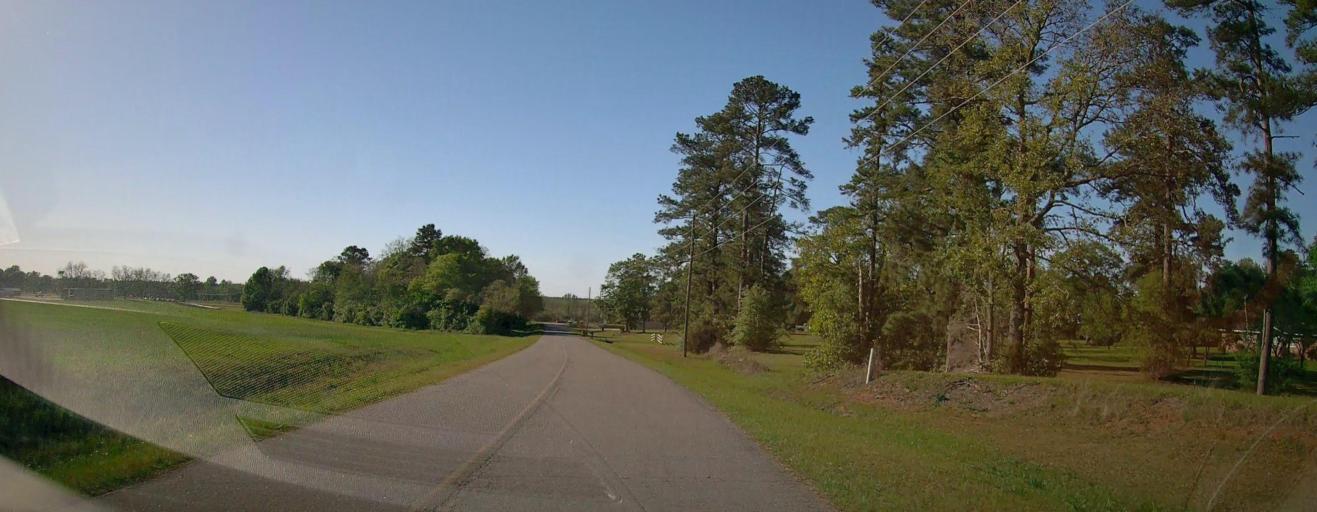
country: US
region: Georgia
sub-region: Houston County
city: Perry
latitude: 32.4373
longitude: -83.7866
